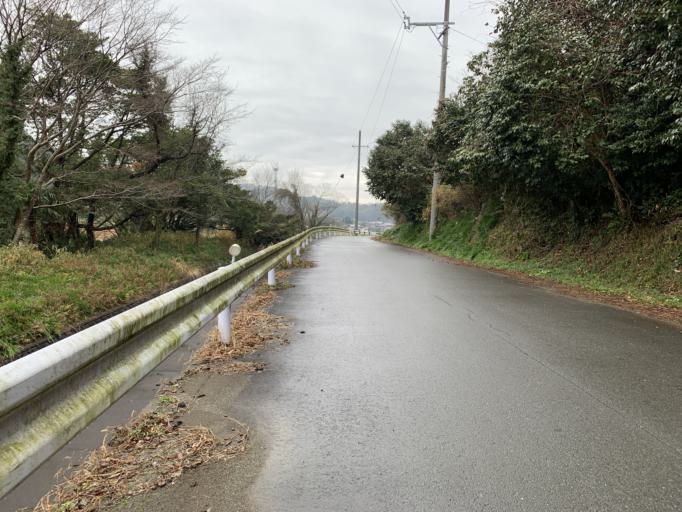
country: JP
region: Mie
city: Ise
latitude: 34.4721
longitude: 136.5471
